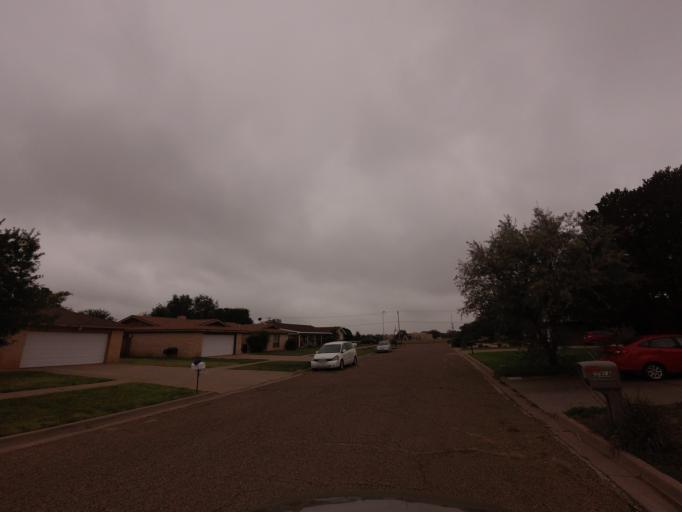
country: US
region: New Mexico
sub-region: Curry County
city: Clovis
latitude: 34.4346
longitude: -103.1918
